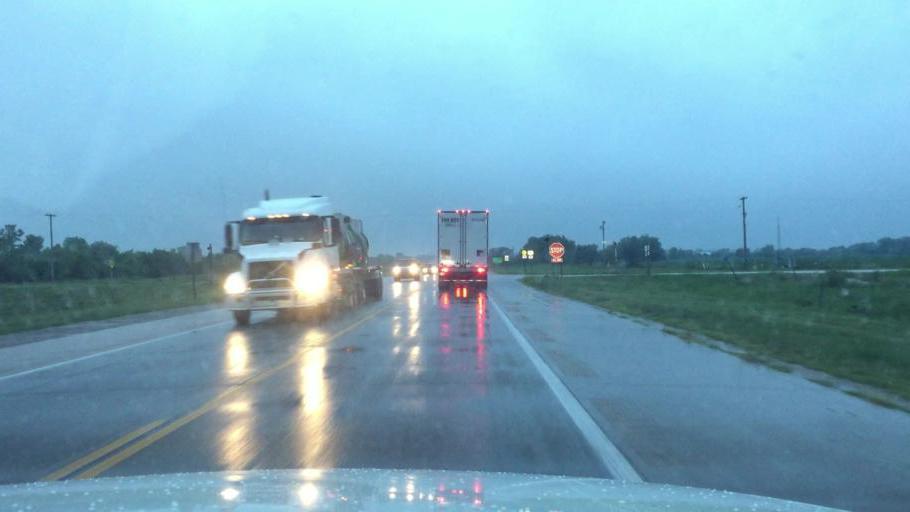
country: US
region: Kansas
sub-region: Neosho County
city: Chanute
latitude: 37.5297
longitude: -95.4716
